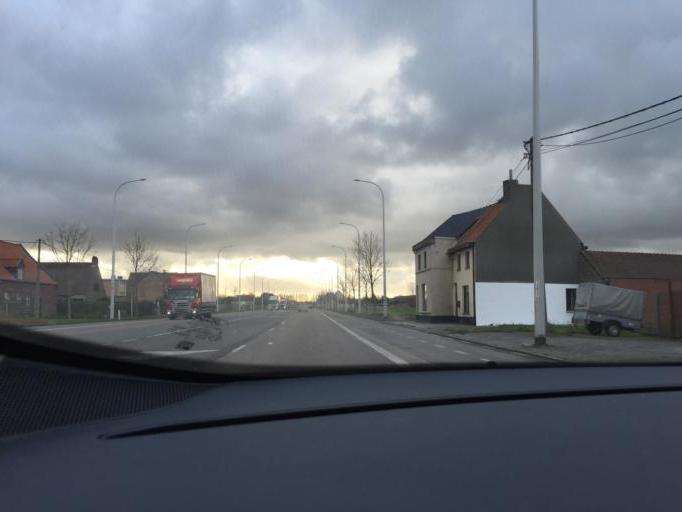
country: BE
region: Flanders
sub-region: Provincie West-Vlaanderen
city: Zeebrugge
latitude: 51.3031
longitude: 3.1900
